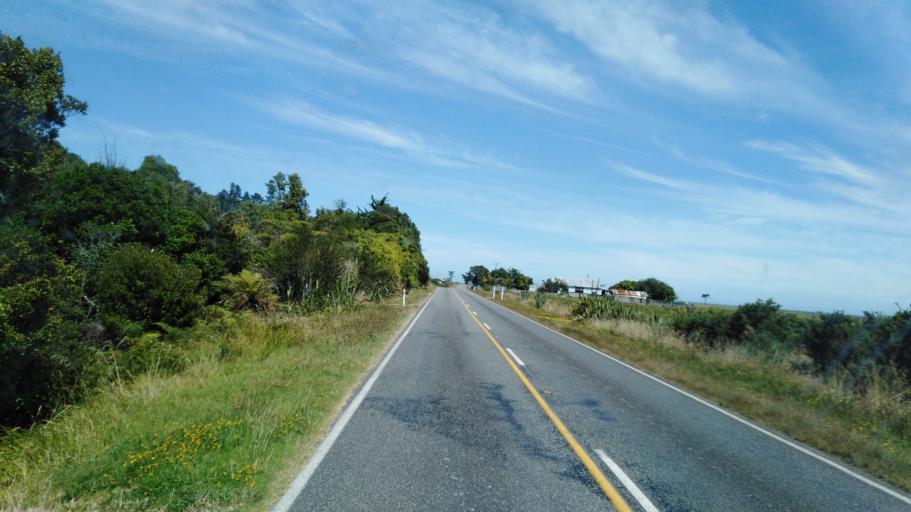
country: NZ
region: West Coast
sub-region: Buller District
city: Westport
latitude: -41.5308
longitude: 171.9414
